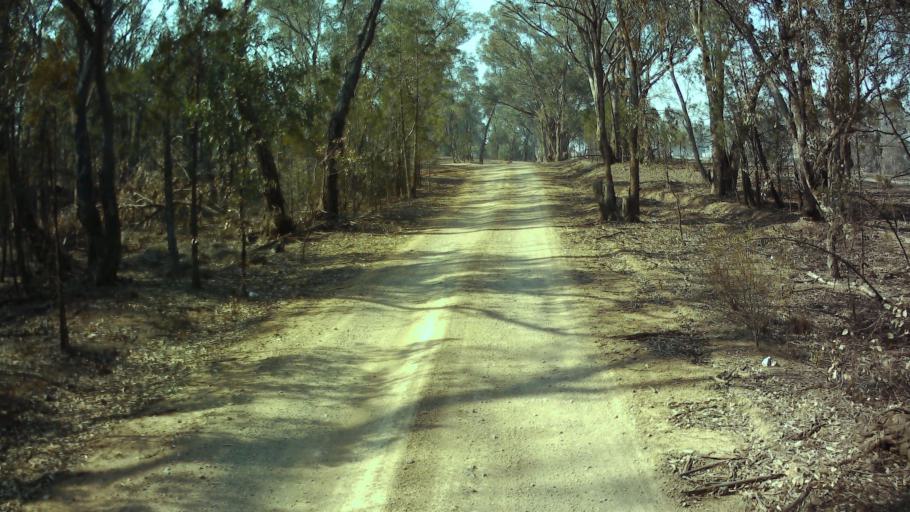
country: AU
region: New South Wales
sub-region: Weddin
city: Grenfell
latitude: -33.8936
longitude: 148.1789
